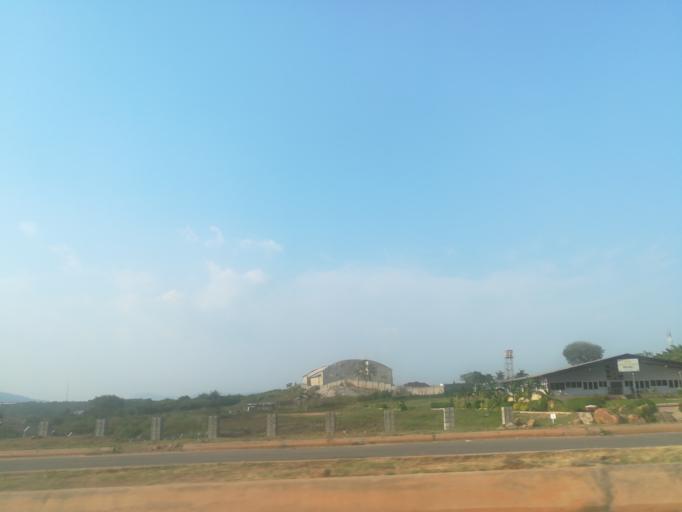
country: NG
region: Abuja Federal Capital Territory
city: Abuja
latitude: 9.0451
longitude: 7.4365
